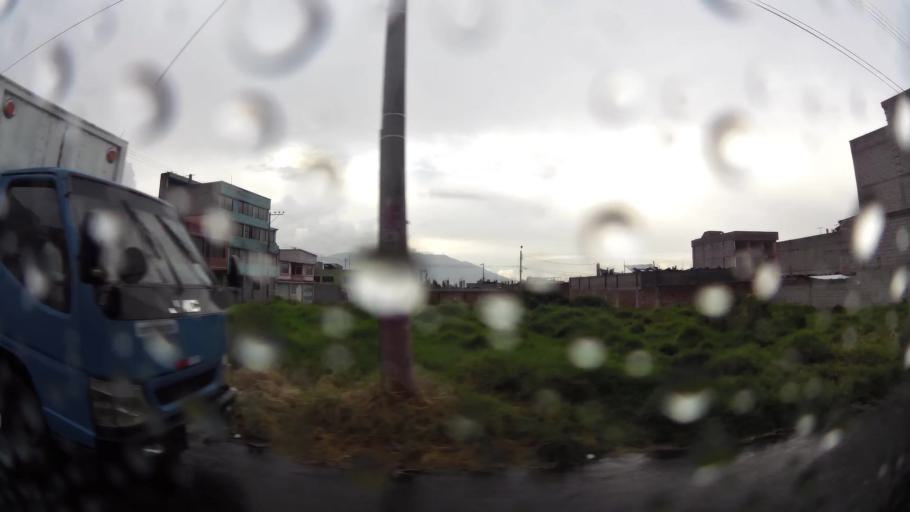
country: EC
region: Pichincha
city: Quito
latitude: -0.3126
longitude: -78.5521
